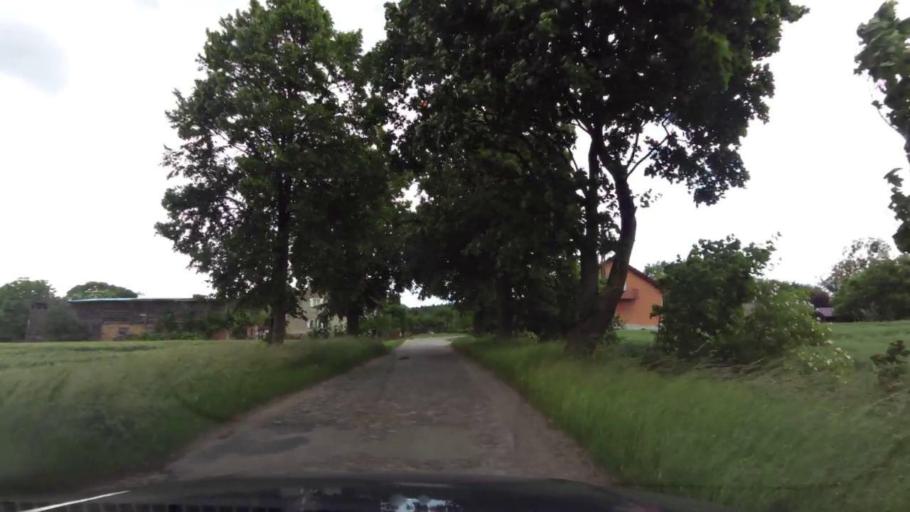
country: PL
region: West Pomeranian Voivodeship
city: Trzcinsko Zdroj
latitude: 52.9759
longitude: 14.7208
